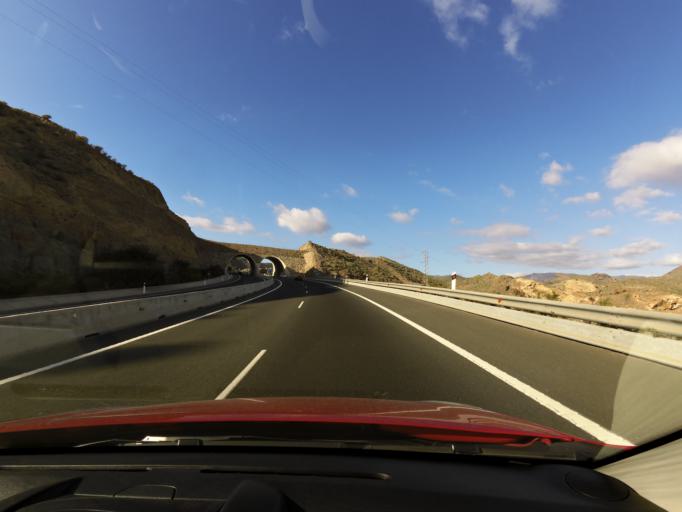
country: ES
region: Canary Islands
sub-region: Provincia de Las Palmas
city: Puerto Rico
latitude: 27.7725
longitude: -15.6744
